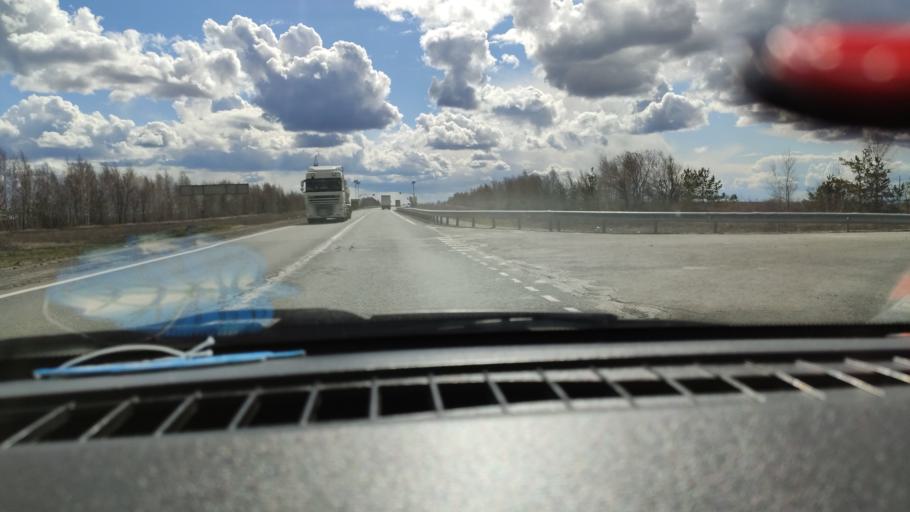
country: RU
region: Saratov
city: Dukhovnitskoye
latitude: 52.8395
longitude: 48.2457
